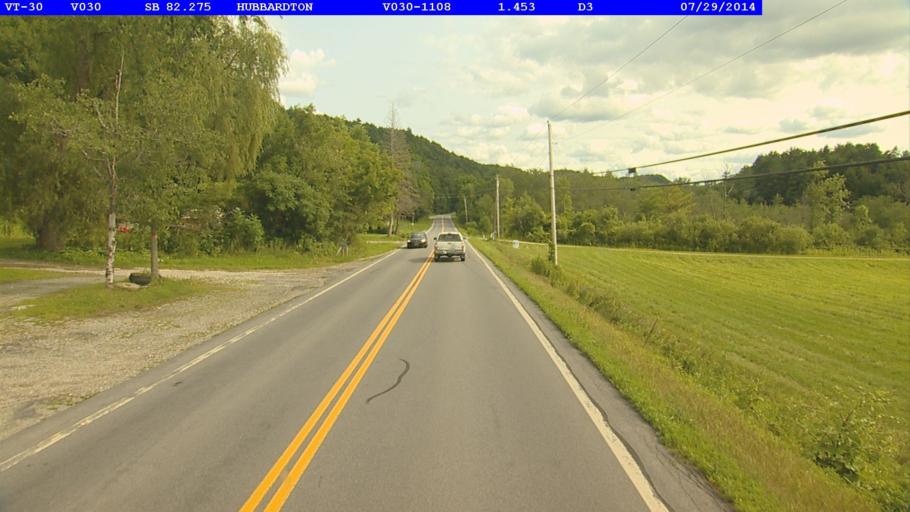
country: US
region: Vermont
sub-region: Rutland County
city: Castleton
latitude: 43.6989
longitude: -73.1852
